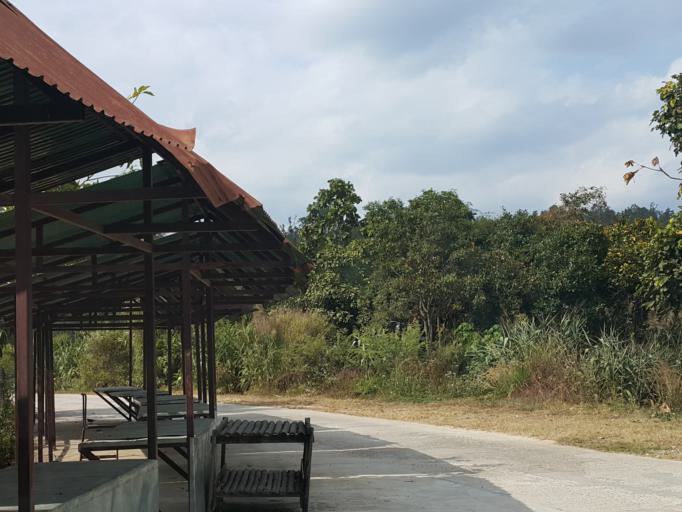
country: TH
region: Chiang Mai
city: Om Koi
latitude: 17.8010
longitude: 98.3640
